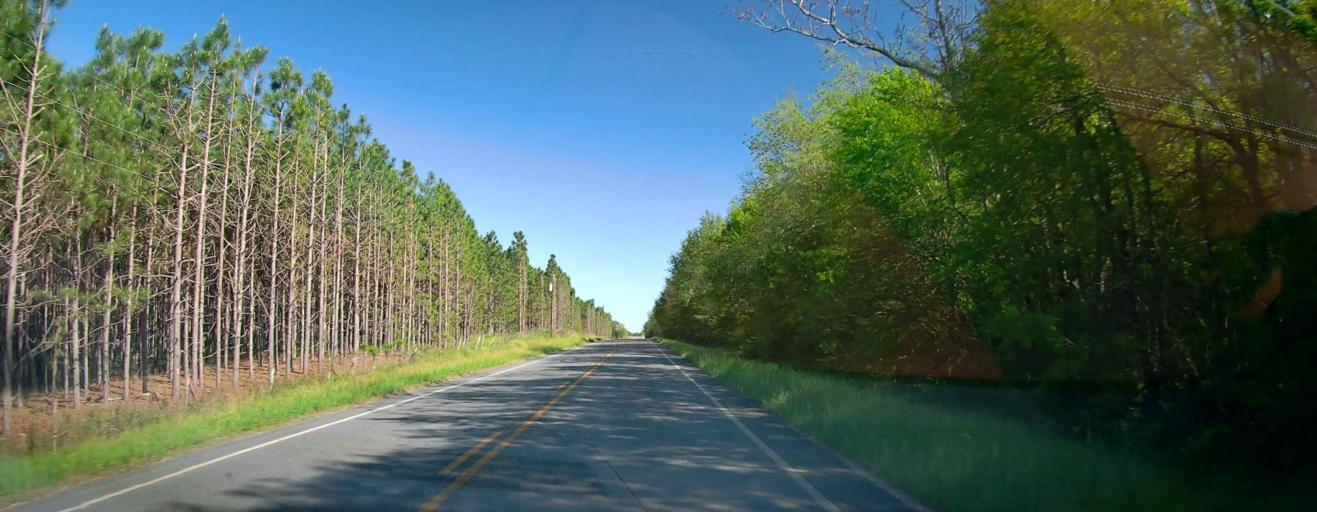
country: US
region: Georgia
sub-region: Wilcox County
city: Rochelle
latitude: 31.9976
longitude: -83.4759
